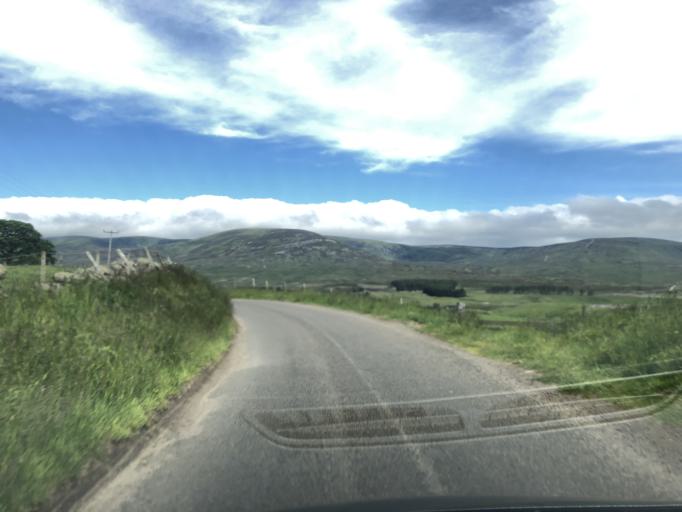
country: GB
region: Scotland
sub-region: Angus
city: Kirriemuir
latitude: 56.8076
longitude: -3.0498
